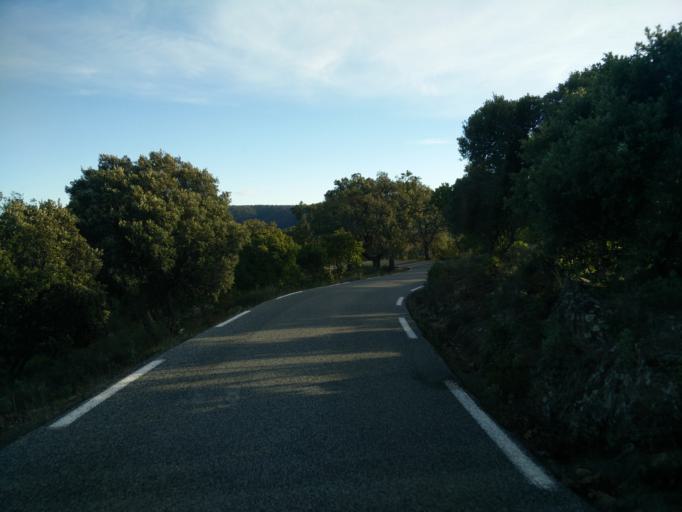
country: FR
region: Provence-Alpes-Cote d'Azur
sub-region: Departement du Var
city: Bormes-les-Mimosas
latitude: 43.1865
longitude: 6.3330
